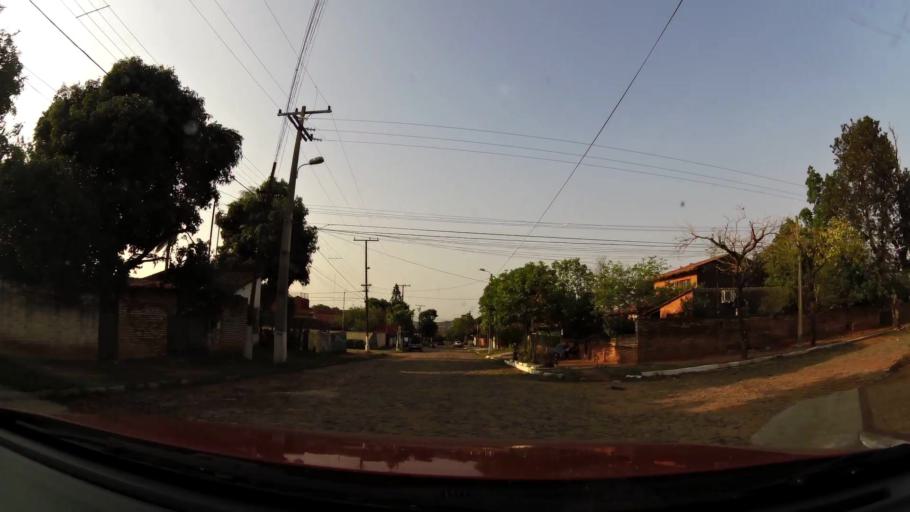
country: PY
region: Central
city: Lambare
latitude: -25.3536
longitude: -57.6107
